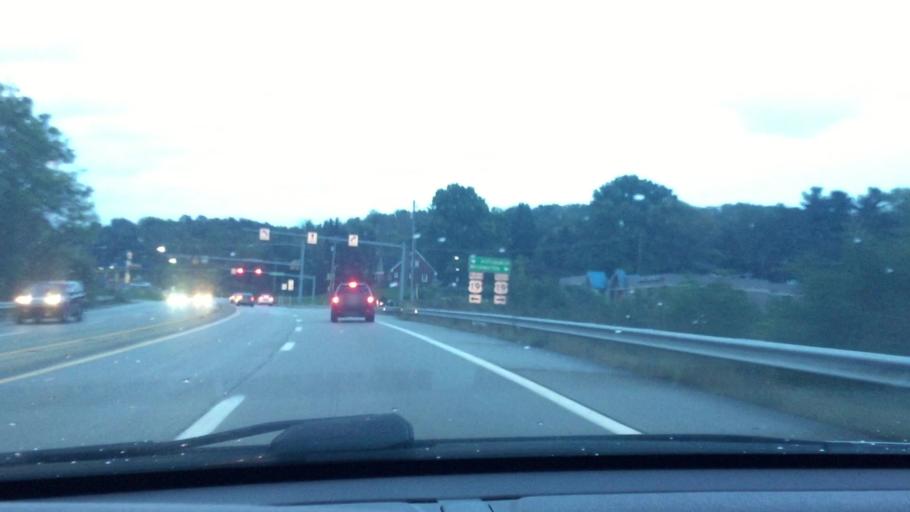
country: US
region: Pennsylvania
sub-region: Washington County
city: McGovern
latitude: 40.2124
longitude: -80.1976
